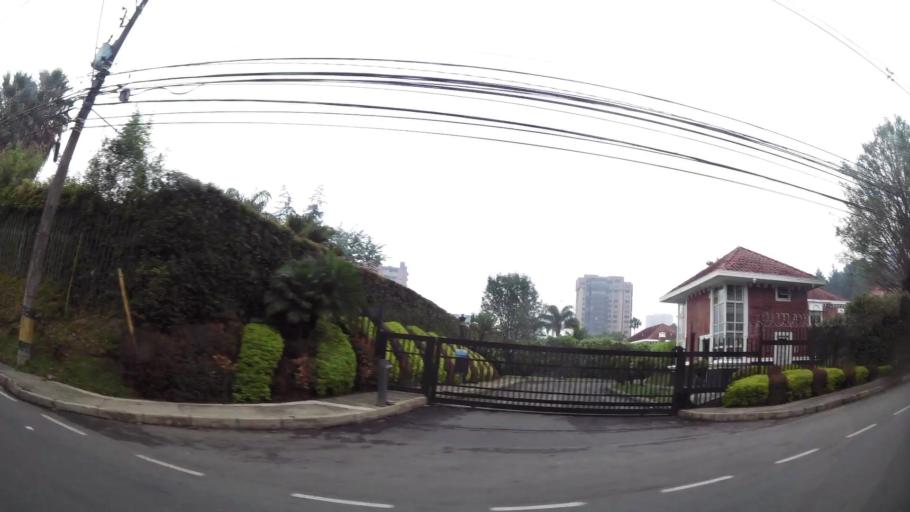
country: CO
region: Antioquia
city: Envigado
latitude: 6.1919
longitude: -75.5562
